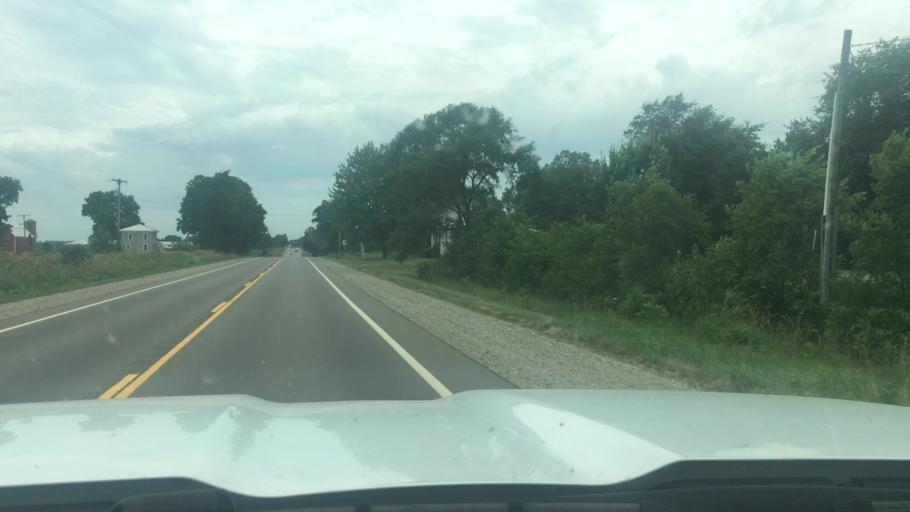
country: US
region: Michigan
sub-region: Clinton County
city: Fowler
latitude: 43.0019
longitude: -84.8029
